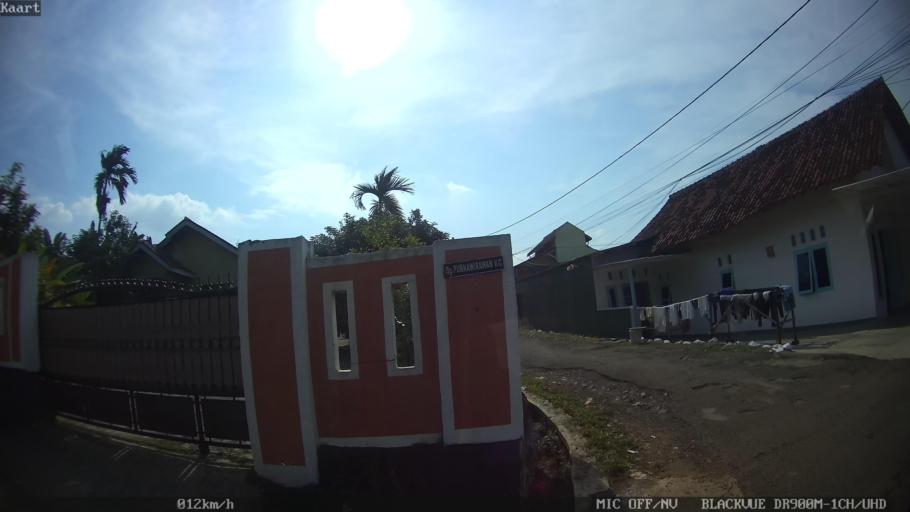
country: ID
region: Lampung
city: Kedaton
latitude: -5.3844
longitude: 105.2303
